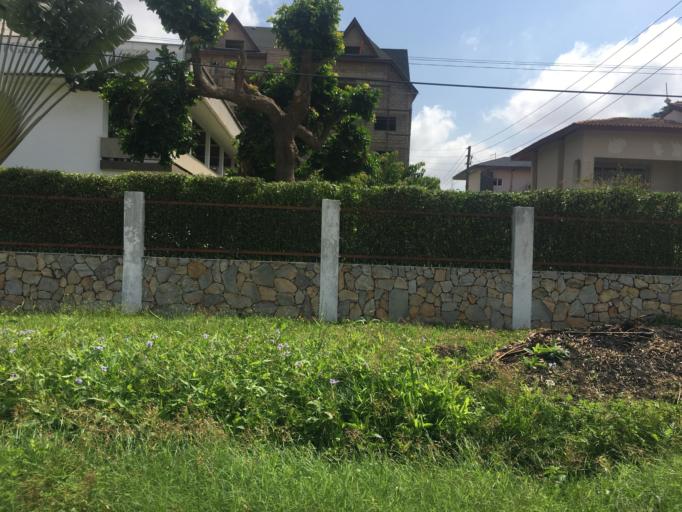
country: GH
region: Greater Accra
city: Medina Estates
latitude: 5.6392
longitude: -0.1652
